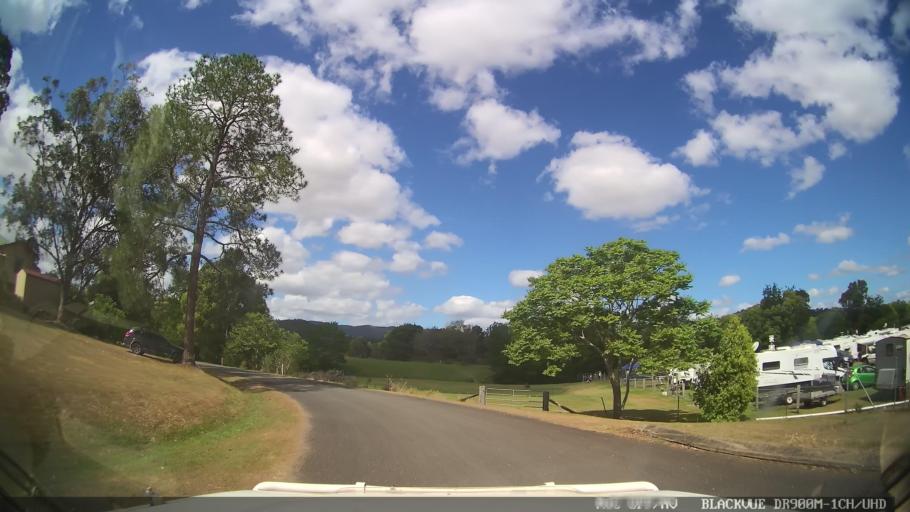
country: AU
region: Queensland
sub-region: Sunshine Coast
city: Yandina
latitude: -26.5969
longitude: 152.7282
